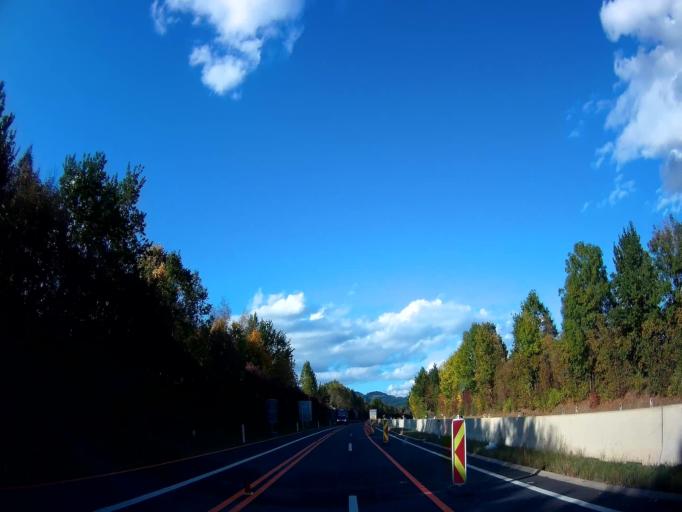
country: AT
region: Carinthia
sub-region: Politischer Bezirk Wolfsberg
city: Wolfsberg
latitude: 46.8267
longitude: 14.8185
